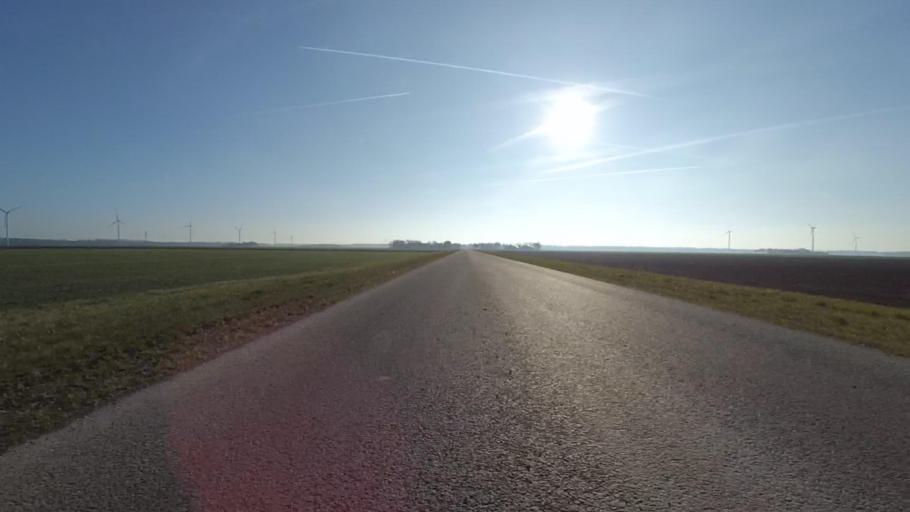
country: NL
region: Utrecht
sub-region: Gemeente Bunschoten
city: Bunschoten
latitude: 52.2998
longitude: 5.4238
